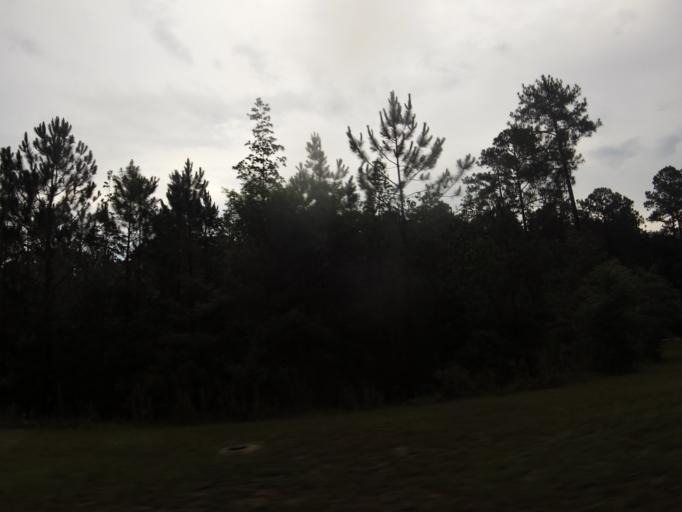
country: US
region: Florida
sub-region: Duval County
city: Jacksonville Beach
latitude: 30.2642
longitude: -81.5002
